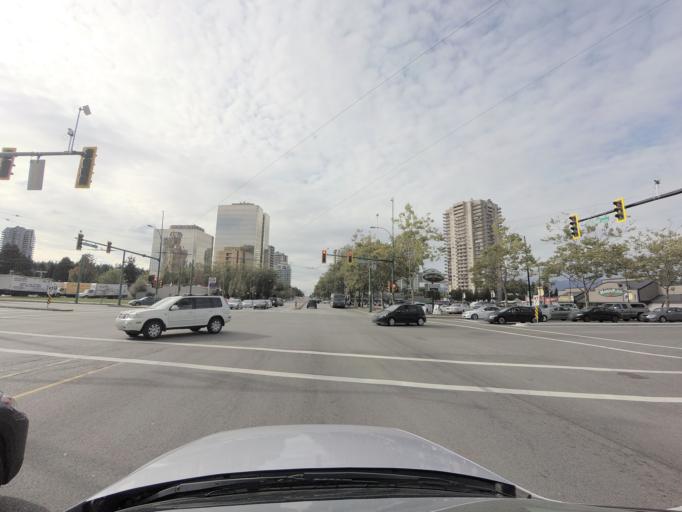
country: CA
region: British Columbia
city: Burnaby
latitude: 49.2304
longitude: -123.0051
